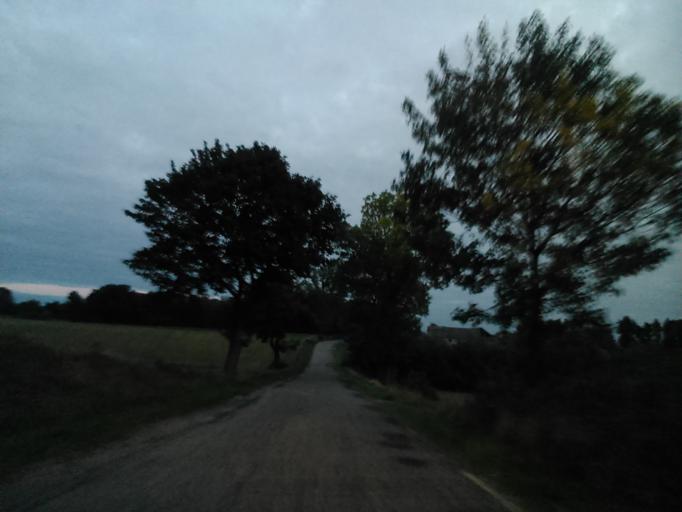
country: PL
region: Kujawsko-Pomorskie
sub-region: Powiat golubsko-dobrzynski
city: Kowalewo Pomorskie
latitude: 53.1270
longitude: 18.9281
